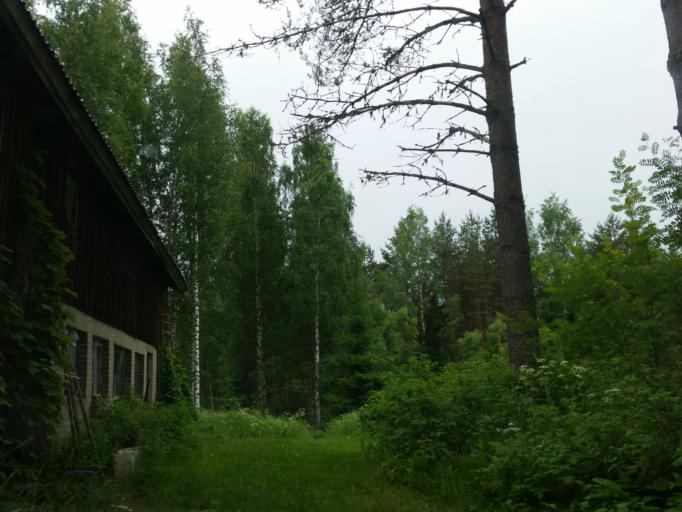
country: FI
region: Northern Savo
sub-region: Koillis-Savo
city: Kaavi
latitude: 62.9835
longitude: 28.7620
